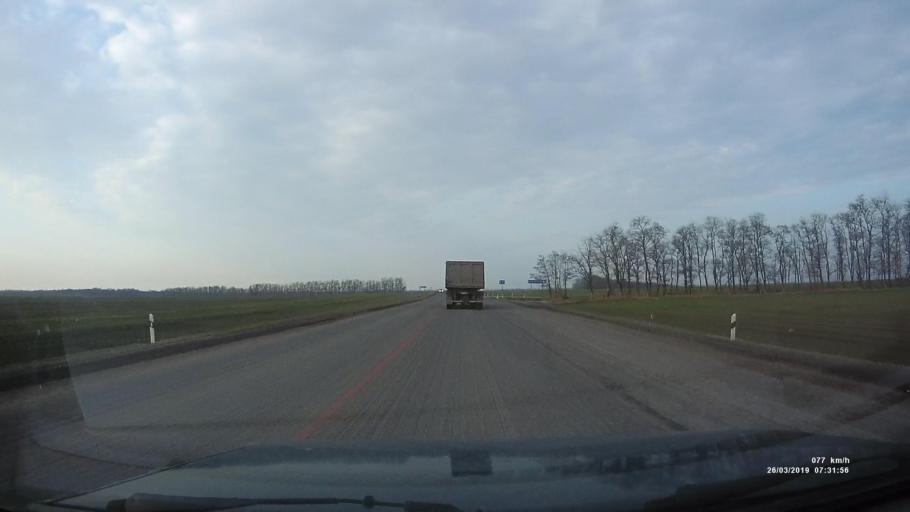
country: RU
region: Rostov
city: Novobessergenovka
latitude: 47.2297
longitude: 38.7834
